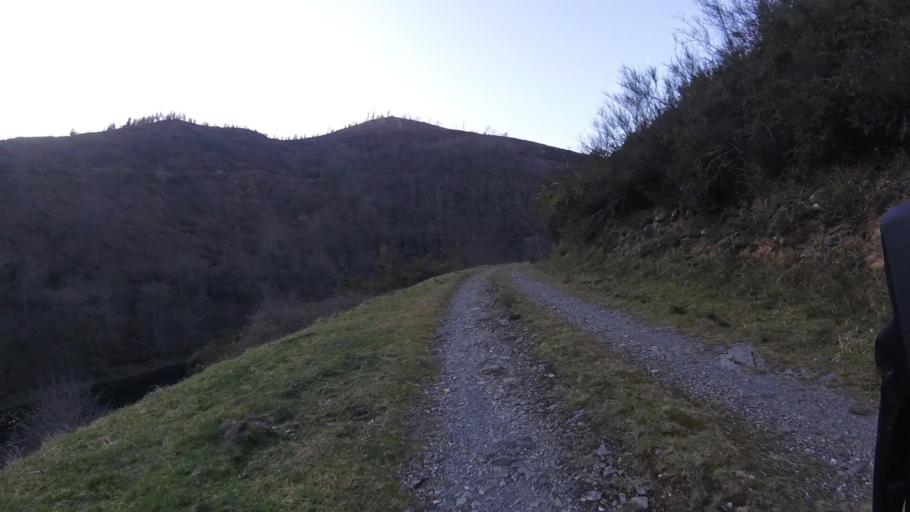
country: ES
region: Navarre
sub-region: Provincia de Navarra
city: Arano
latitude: 43.2125
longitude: -1.8623
